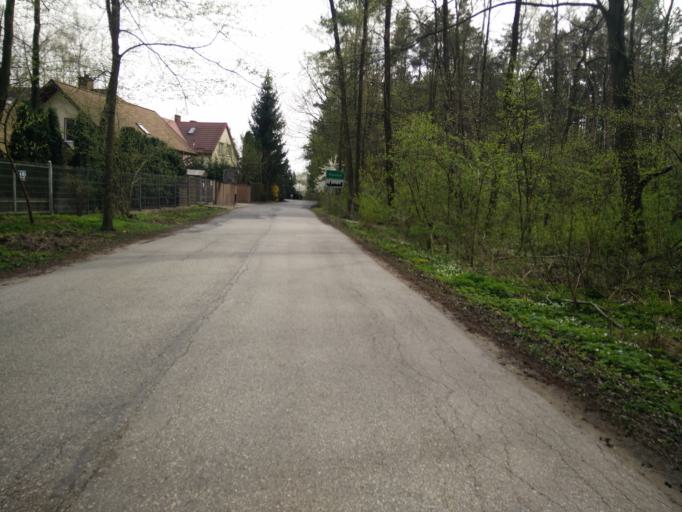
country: PL
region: Masovian Voivodeship
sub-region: Powiat warszawski zachodni
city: Stare Babice
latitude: 52.2821
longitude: 20.8418
